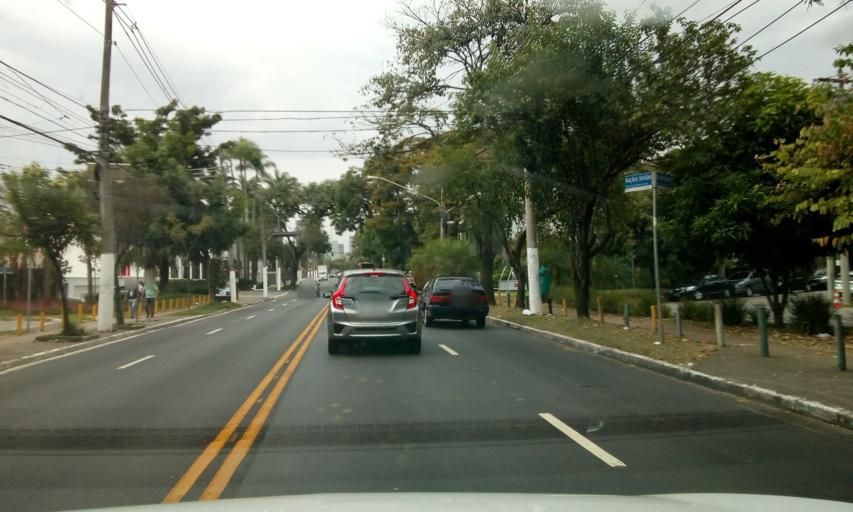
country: BR
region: Sao Paulo
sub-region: Sao Paulo
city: Sao Paulo
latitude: -23.5755
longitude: -46.6783
